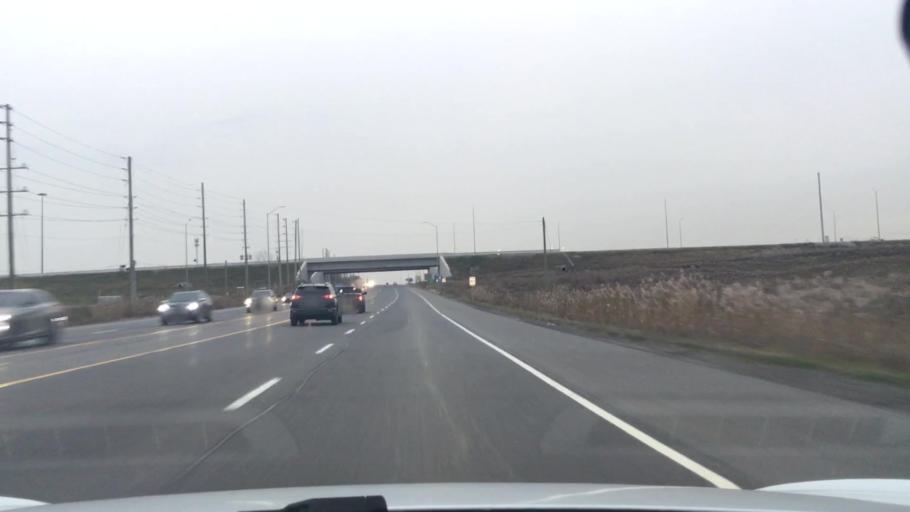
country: CA
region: Ontario
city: Ajax
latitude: 43.9436
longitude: -79.0033
